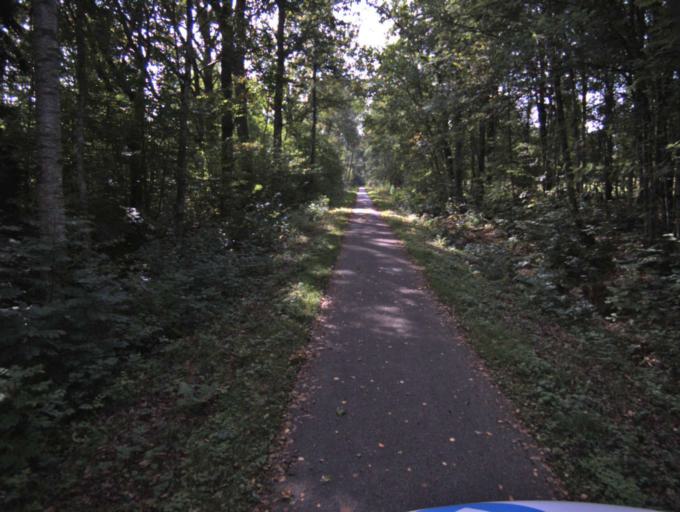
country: SE
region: Vaestra Goetaland
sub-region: Tranemo Kommun
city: Limmared
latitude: 57.6488
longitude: 13.3605
